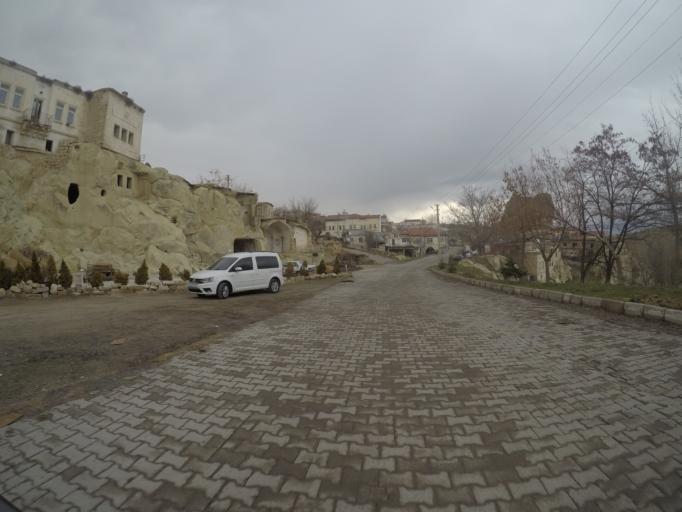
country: TR
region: Nevsehir
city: Goereme
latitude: 38.6199
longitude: 34.8668
